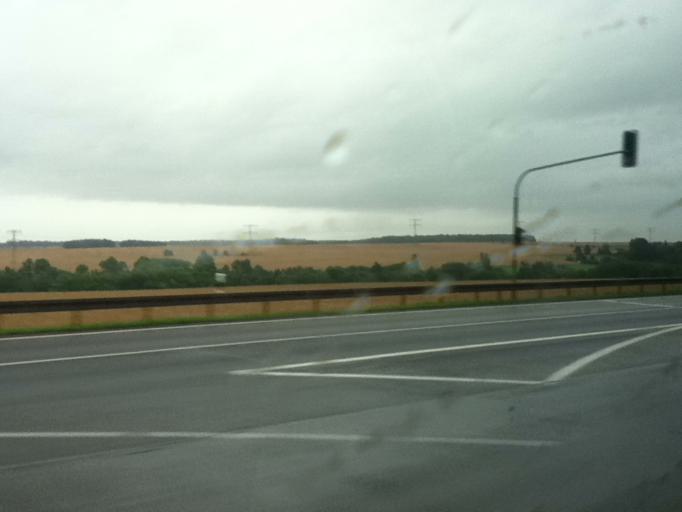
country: DE
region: Thuringia
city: Kirchheim
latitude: 50.9104
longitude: 11.0145
